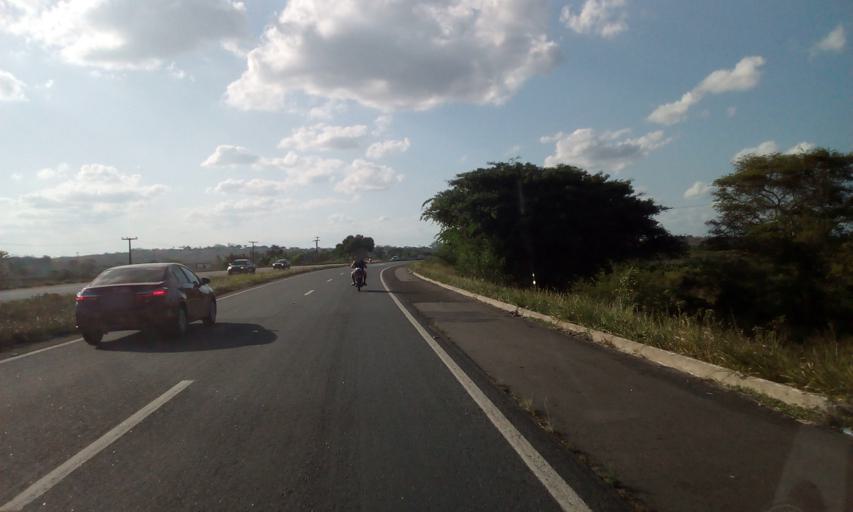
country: BR
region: Paraiba
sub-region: Pilar
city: Pilar
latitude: -7.1910
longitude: -35.1835
